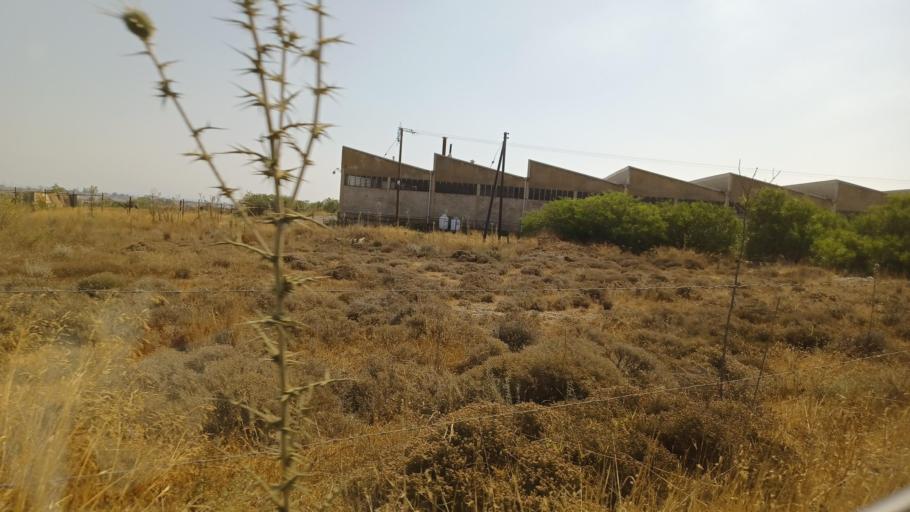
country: CY
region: Ammochostos
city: Deryneia
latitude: 35.0715
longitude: 33.9538
